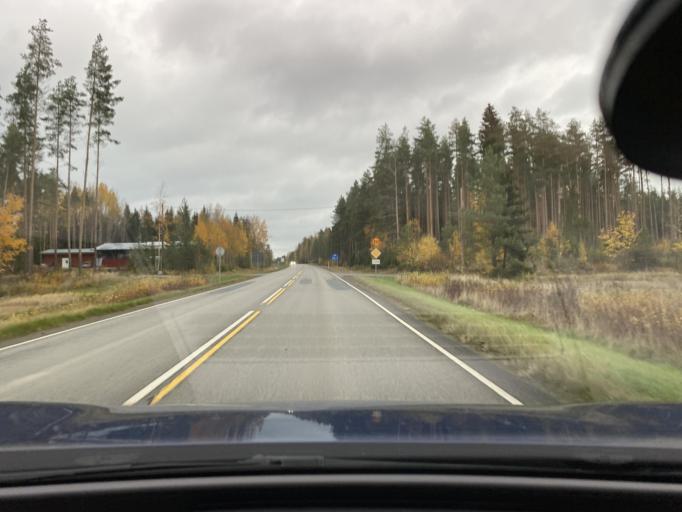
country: FI
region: Varsinais-Suomi
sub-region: Loimaa
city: Ylaene
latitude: 60.8883
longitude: 22.4030
